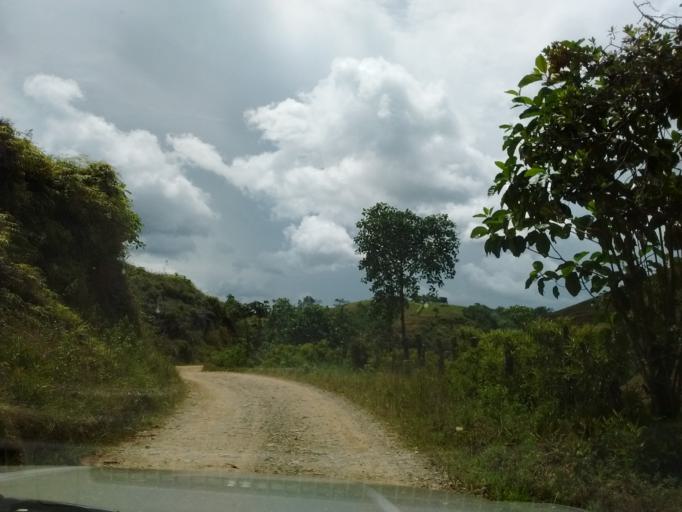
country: CO
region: Cauca
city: Villa Rica
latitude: 2.6051
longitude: -76.7529
